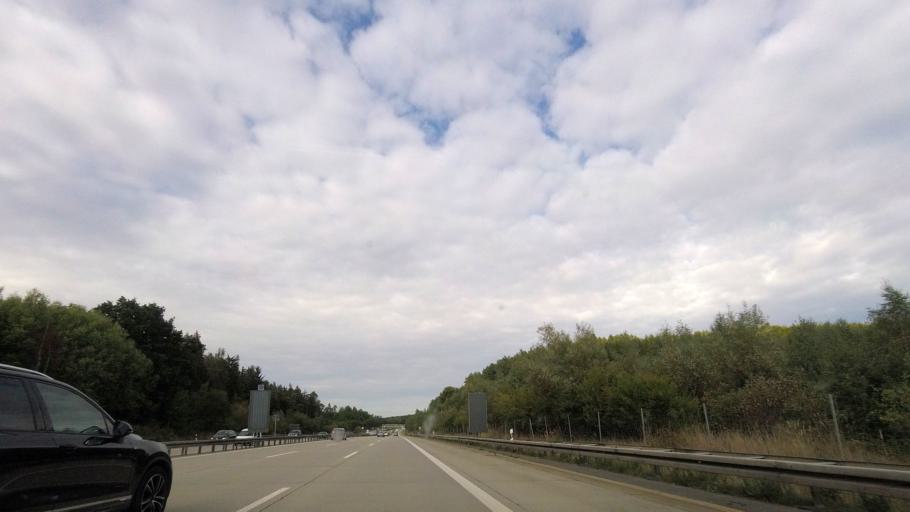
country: DE
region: Thuringia
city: Hainspitz
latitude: 50.9490
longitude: 11.8352
